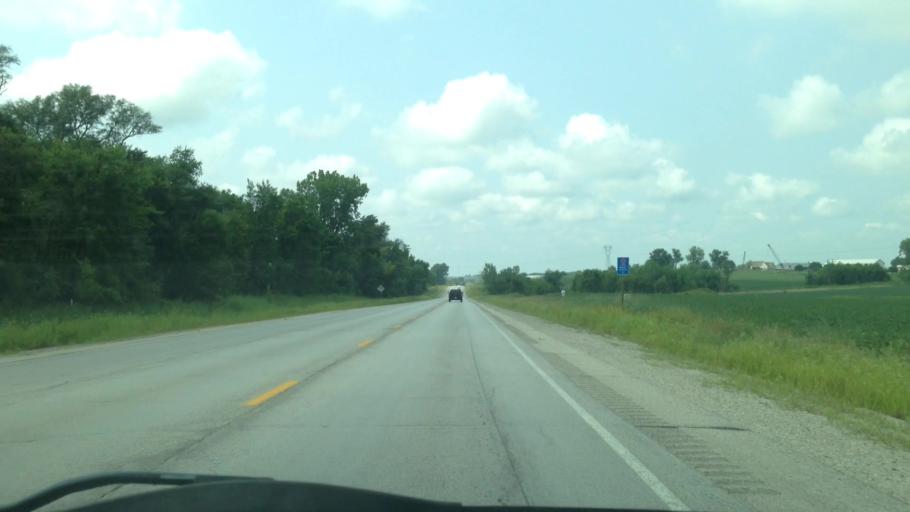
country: US
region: Iowa
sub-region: Benton County
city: Walford
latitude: 41.8927
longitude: -91.8143
